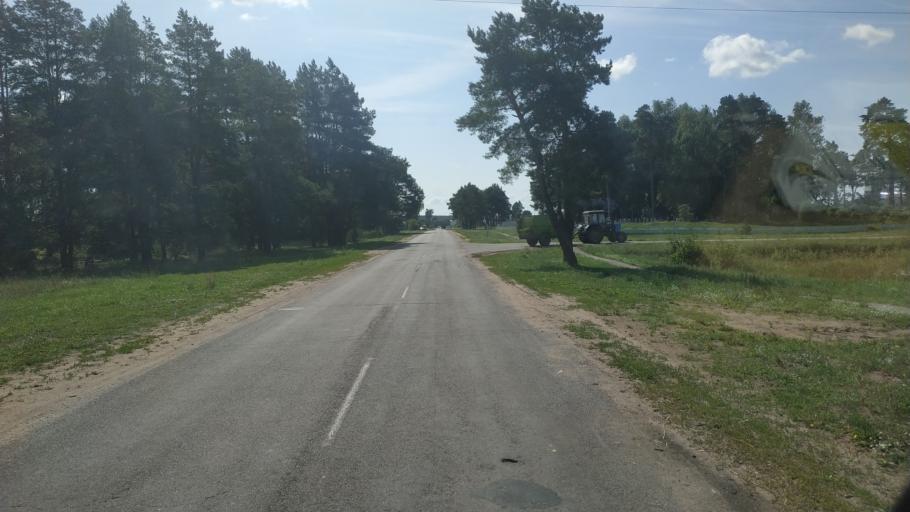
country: BY
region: Mogilev
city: Poselok Voskhod
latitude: 53.7114
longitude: 30.4969
